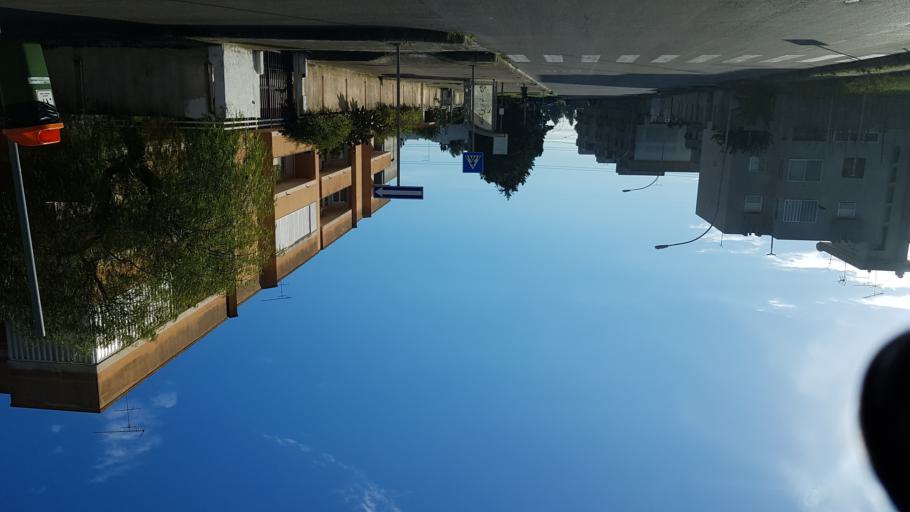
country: IT
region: Apulia
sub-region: Provincia di Brindisi
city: La Rosa
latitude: 40.6052
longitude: 17.9516
